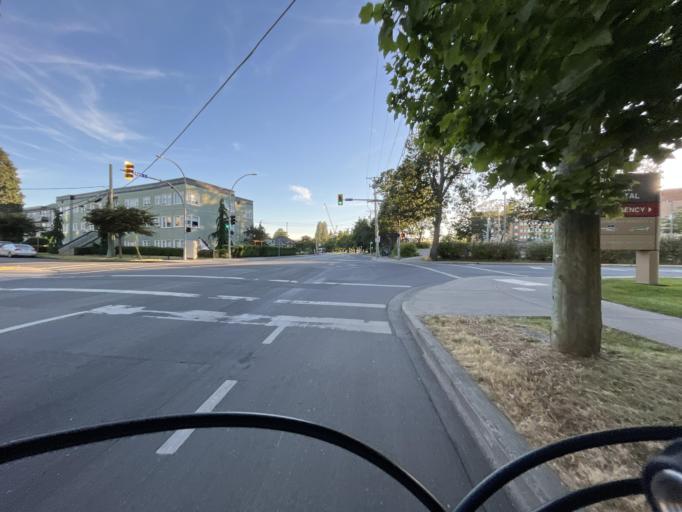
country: CA
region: British Columbia
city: Oak Bay
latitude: 48.4316
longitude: -123.3255
